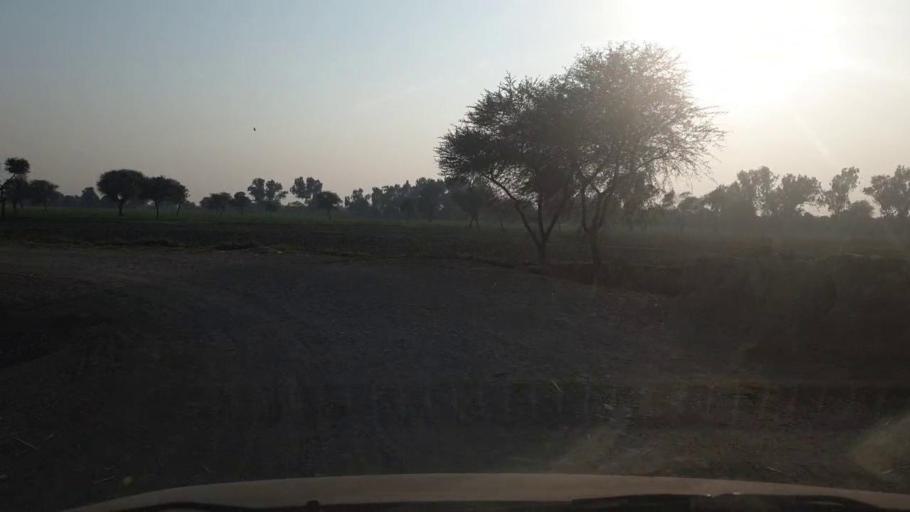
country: PK
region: Sindh
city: Mirwah Gorchani
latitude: 25.3620
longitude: 69.1521
